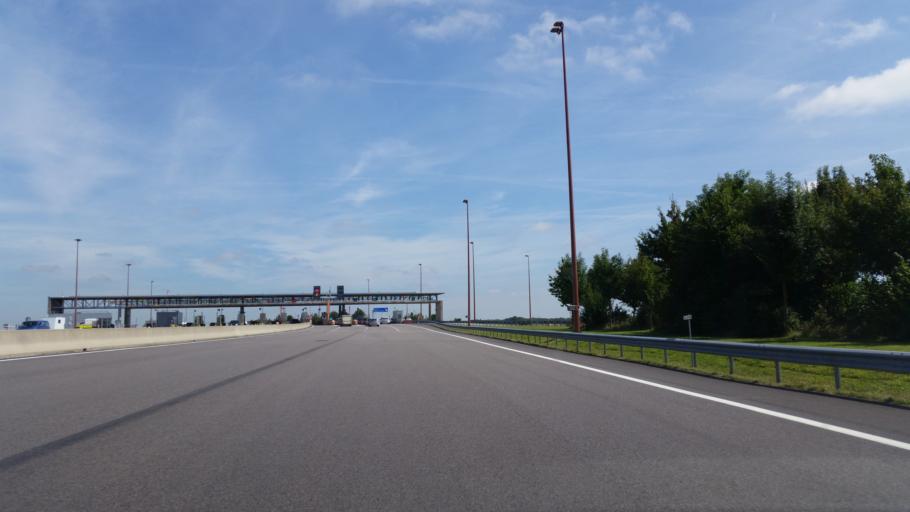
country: FR
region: Haute-Normandie
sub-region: Departement de la Seine-Maritime
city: Aumale
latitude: 49.7583
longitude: 1.7008
